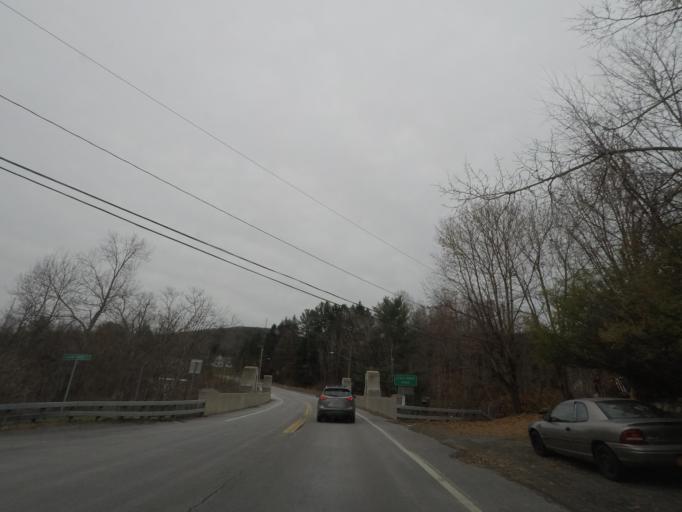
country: US
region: Massachusetts
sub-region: Berkshire County
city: Williamstown
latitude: 42.7492
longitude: -73.3396
